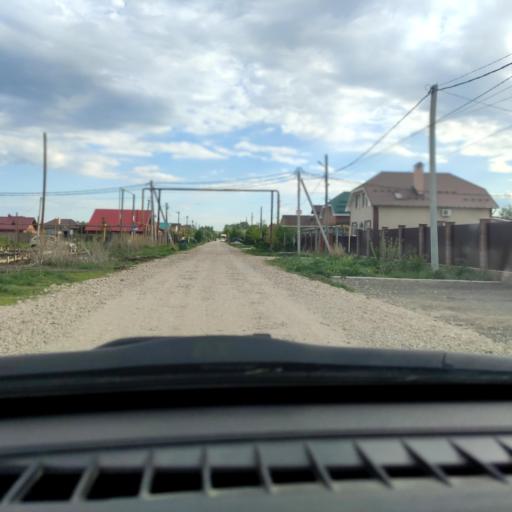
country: RU
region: Samara
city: Tol'yatti
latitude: 53.5637
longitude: 49.4071
